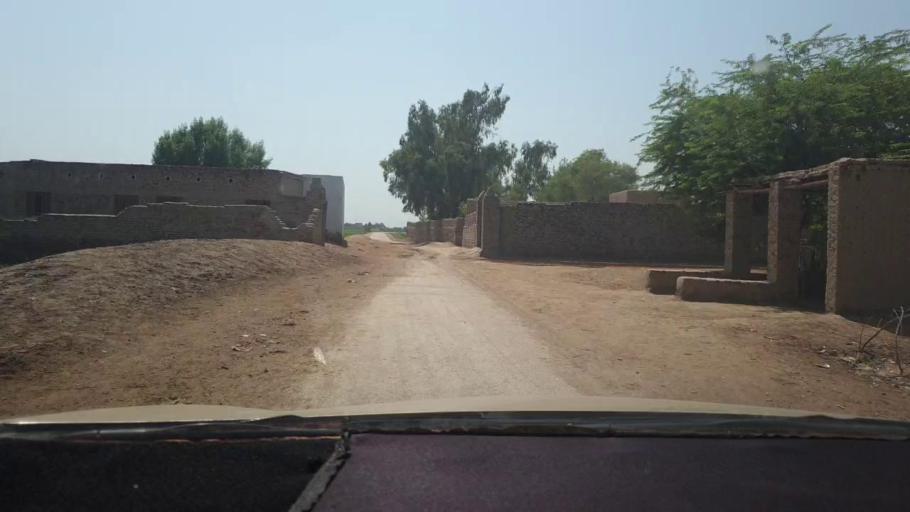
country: PK
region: Sindh
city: Miro Khan
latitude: 27.6686
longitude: 68.0988
